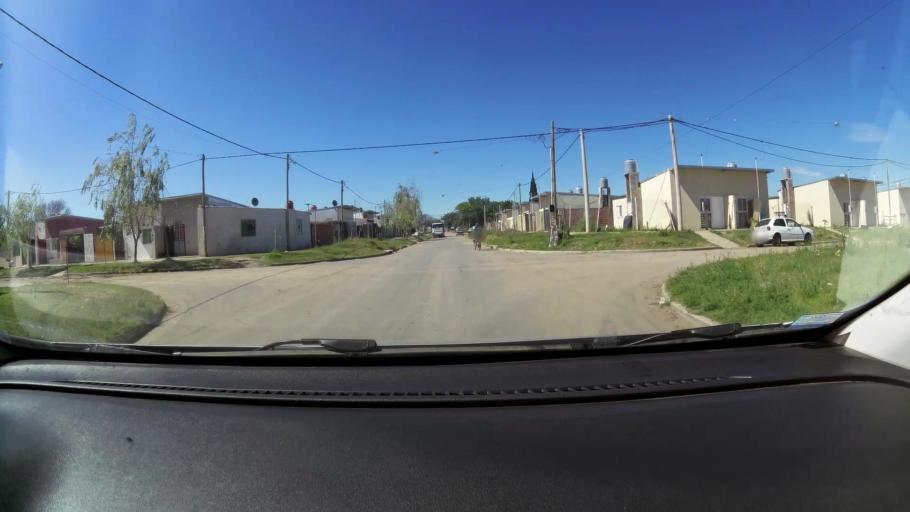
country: AR
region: Santa Fe
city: Perez
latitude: -32.9756
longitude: -60.7044
